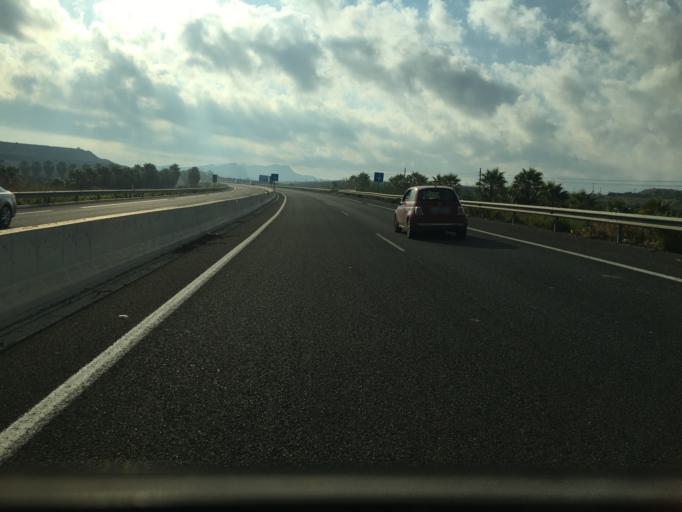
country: ES
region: Murcia
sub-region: Murcia
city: Beniel
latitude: 37.9951
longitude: -1.0000
